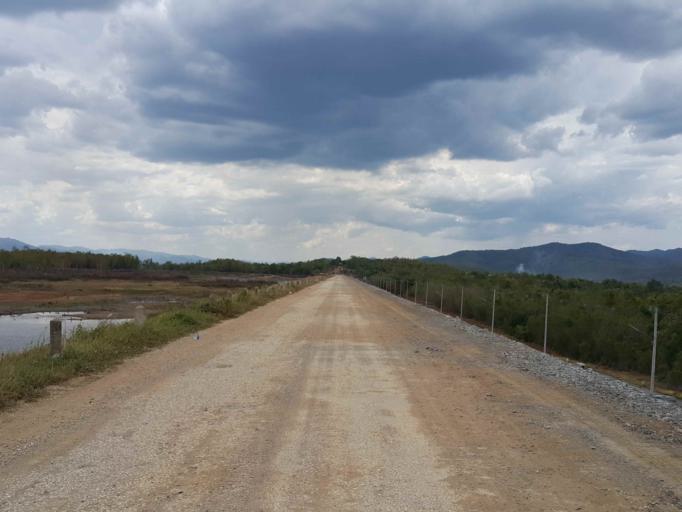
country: TH
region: Sukhothai
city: Thung Saliam
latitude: 17.3169
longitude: 99.4242
